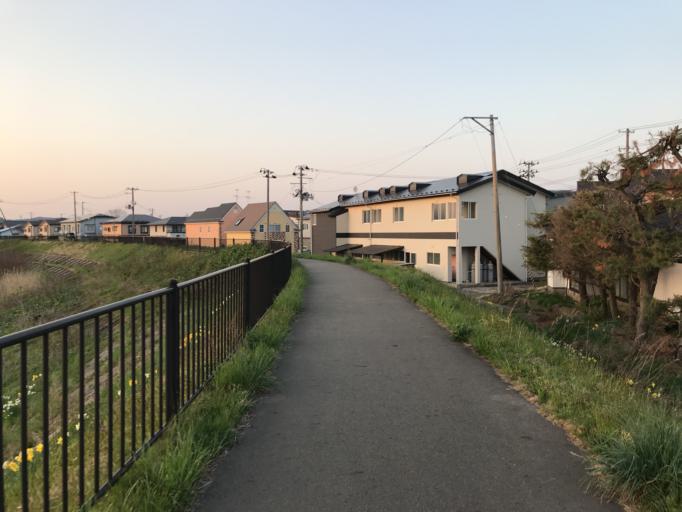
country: JP
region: Akita
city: Akita
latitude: 39.7294
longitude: 140.1278
